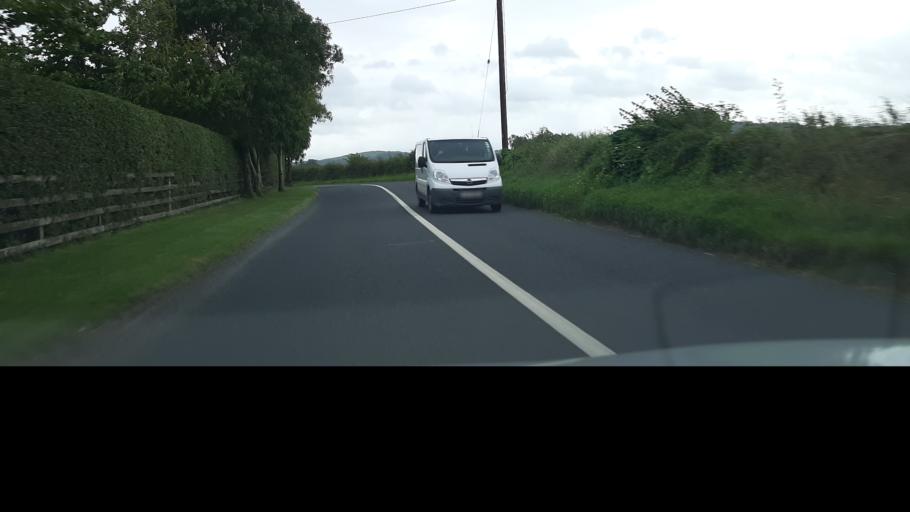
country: IE
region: Leinster
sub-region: Kildare
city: Rathangan
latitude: 53.2153
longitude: -6.9639
